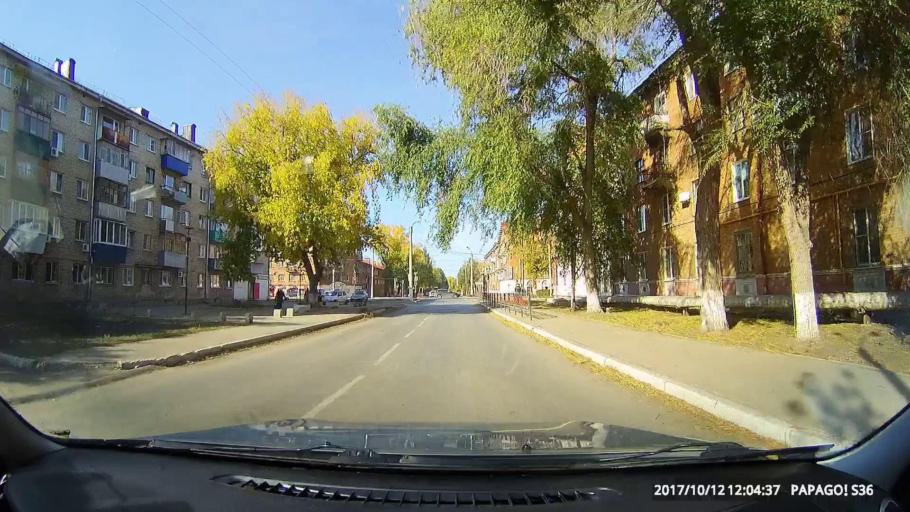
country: RU
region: Samara
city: Chapayevsk
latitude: 52.9788
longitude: 49.7144
